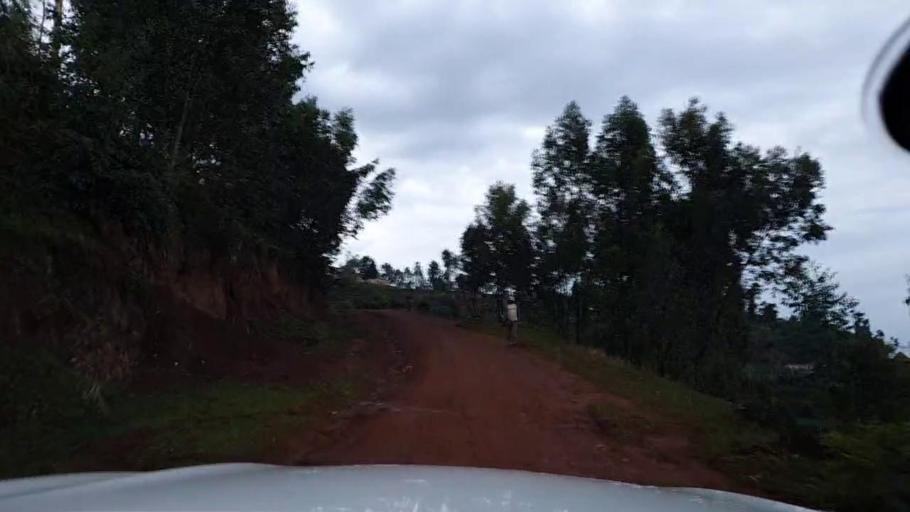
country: BI
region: Kayanza
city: Kayanza
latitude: -2.7152
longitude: 29.5420
